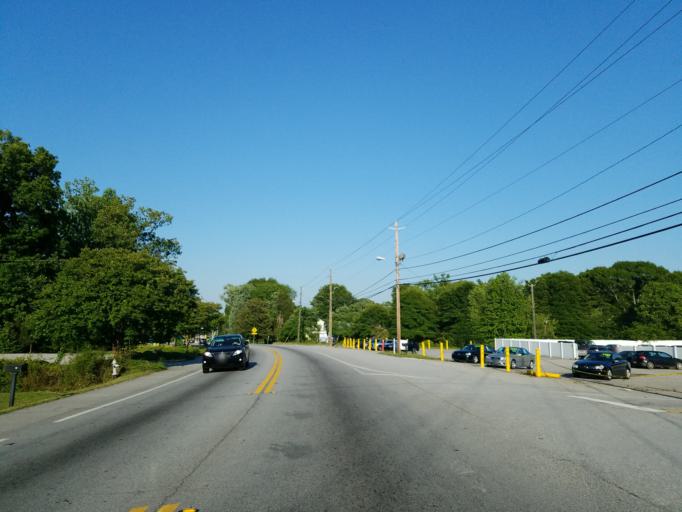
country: US
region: Georgia
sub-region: Douglas County
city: Lithia Springs
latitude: 33.7959
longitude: -84.6475
